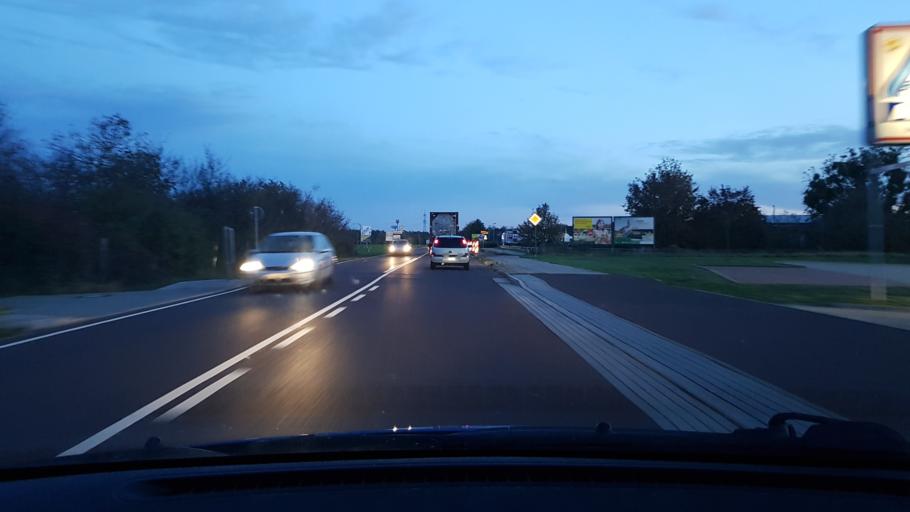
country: DE
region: Saxony-Anhalt
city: Zerbst
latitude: 51.9545
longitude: 12.1029
